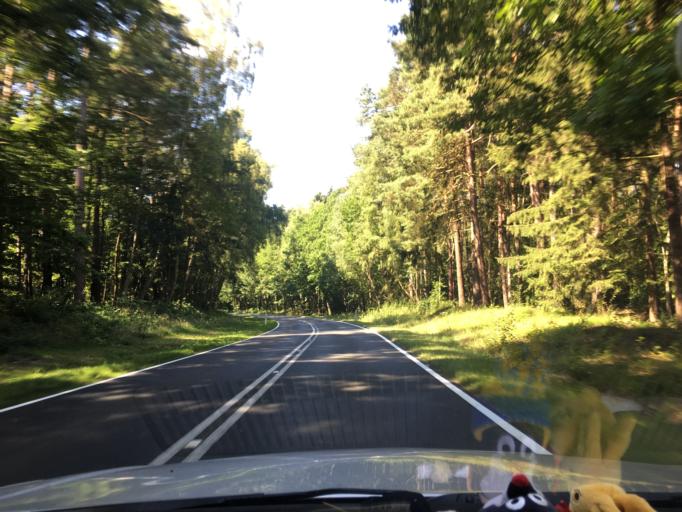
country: PL
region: West Pomeranian Voivodeship
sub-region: Powiat kamienski
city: Dziwnow
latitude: 53.9910
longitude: 14.6347
